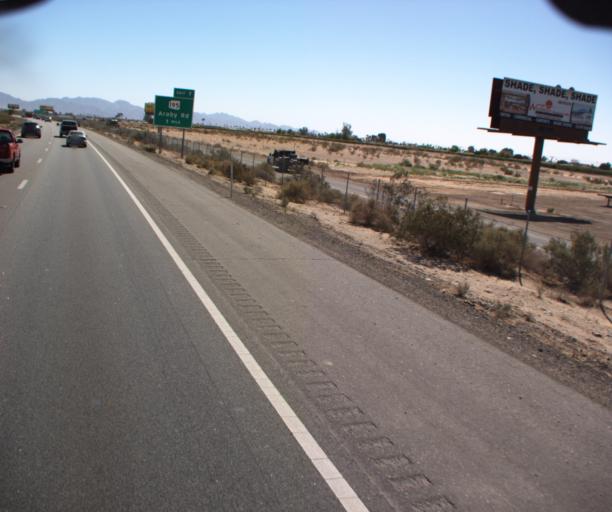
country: US
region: Arizona
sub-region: Yuma County
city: Yuma
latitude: 32.6772
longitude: -114.5444
